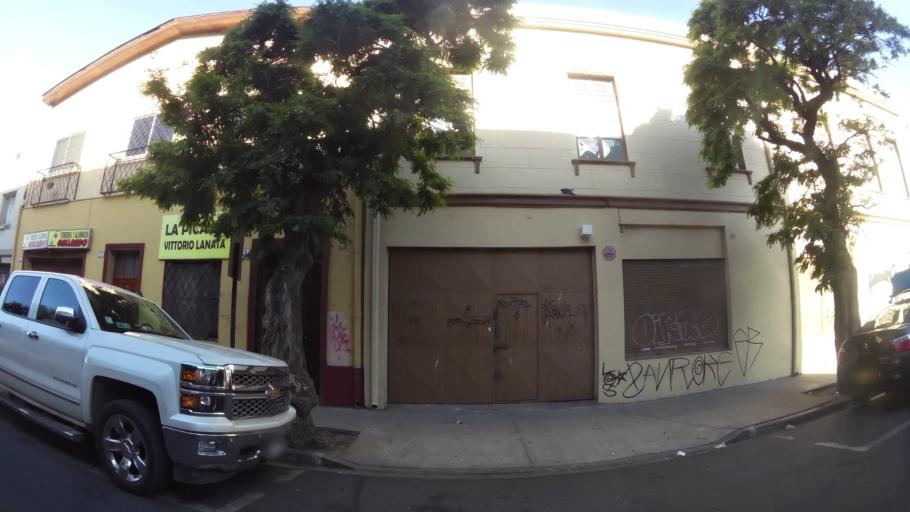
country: CL
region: Valparaiso
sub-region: Provincia de Valparaiso
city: Valparaiso
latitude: -33.0471
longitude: -71.6098
